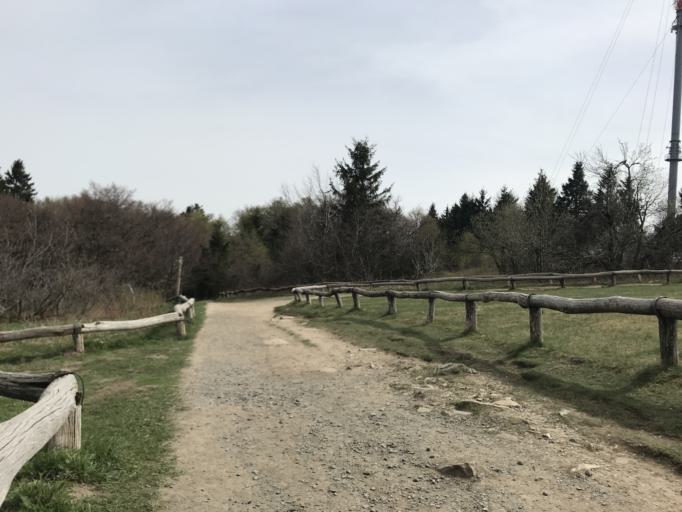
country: DE
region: Hesse
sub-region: Regierungsbezirk Darmstadt
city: Schmitten
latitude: 50.2338
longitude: 8.4588
